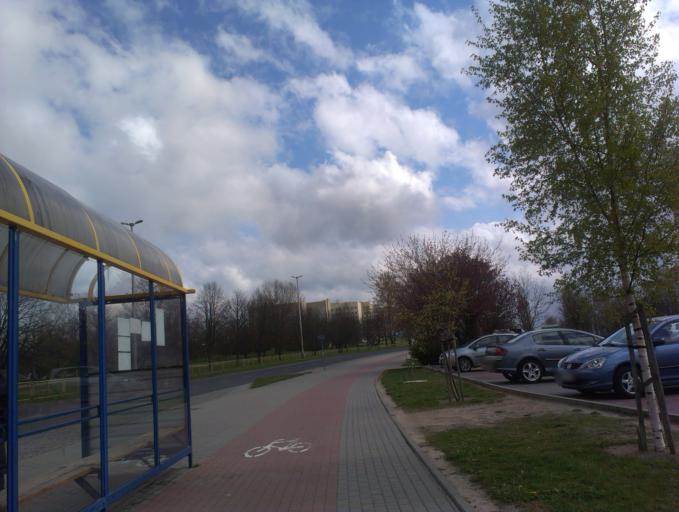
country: PL
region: West Pomeranian Voivodeship
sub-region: Koszalin
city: Koszalin
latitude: 54.2052
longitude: 16.1922
